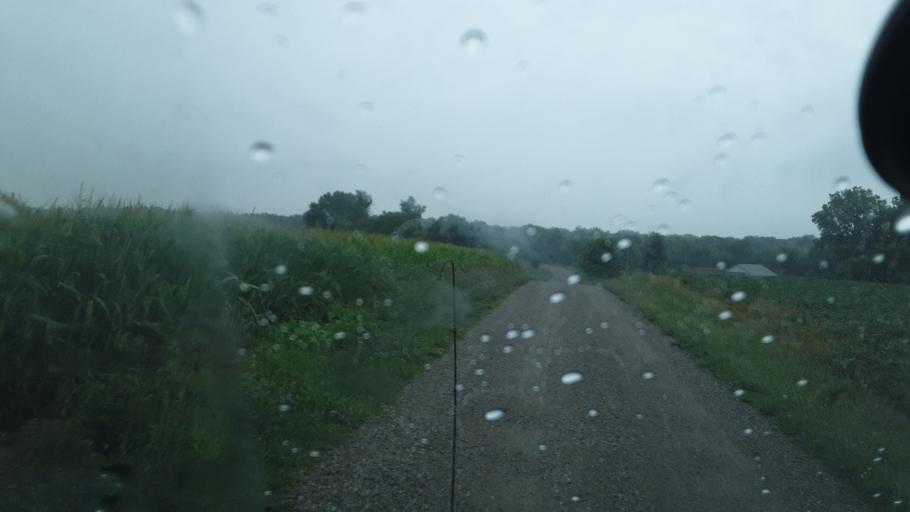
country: US
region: Ohio
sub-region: Williams County
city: Edgerton
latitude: 41.4116
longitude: -84.7988
